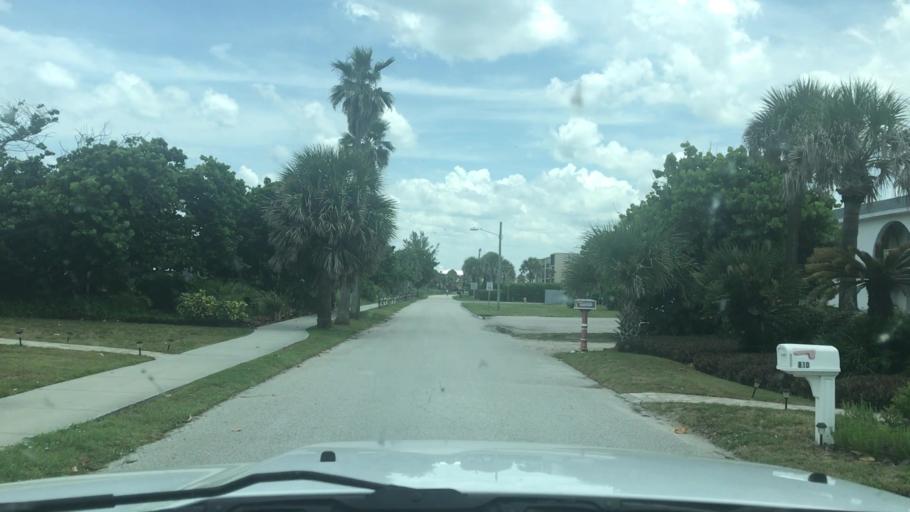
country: US
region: Florida
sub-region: Brevard County
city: Indialantic
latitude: 28.0865
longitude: -80.5641
